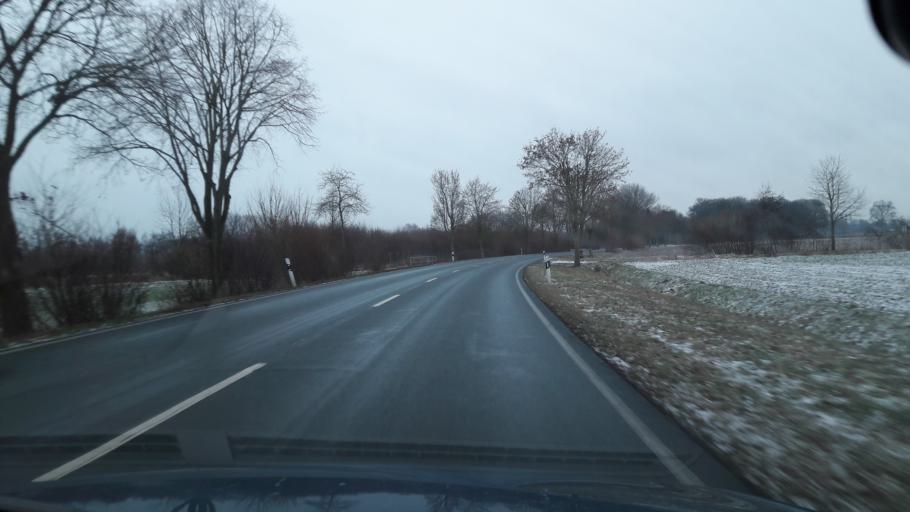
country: DE
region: North Rhine-Westphalia
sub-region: Regierungsbezirk Munster
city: Wadersloh
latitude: 51.7263
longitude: 8.2643
